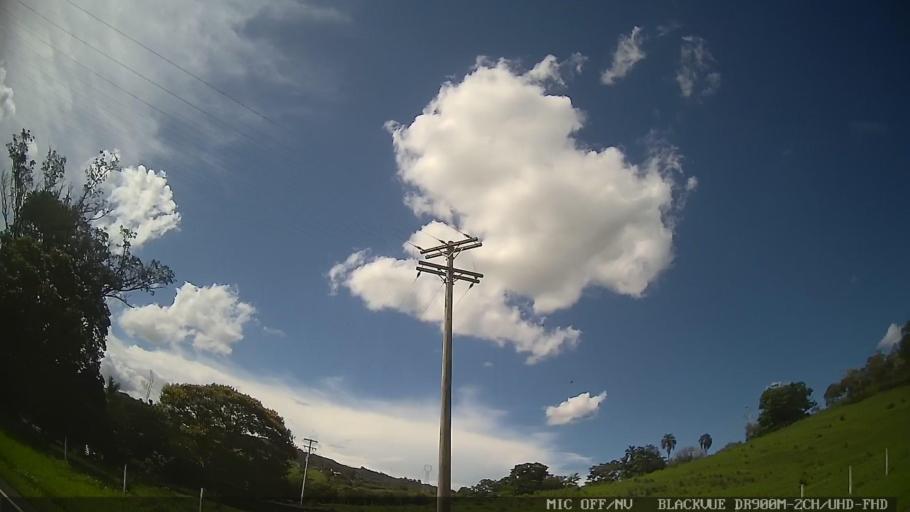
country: BR
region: Sao Paulo
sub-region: Pedreira
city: Pedreira
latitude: -22.7341
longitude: -46.8651
